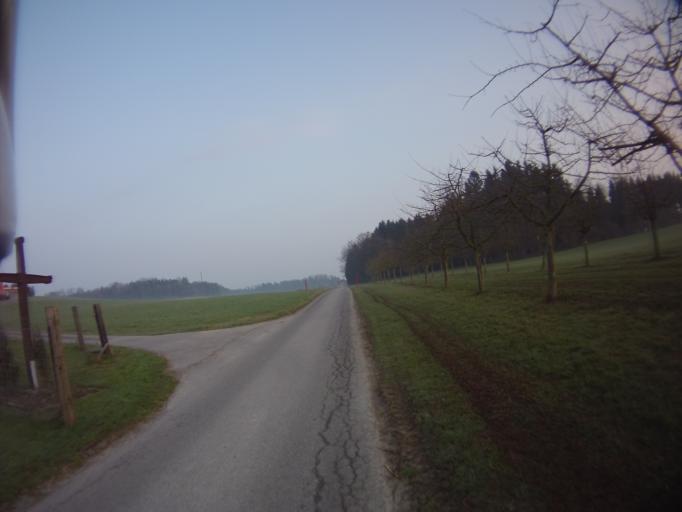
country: CH
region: Zug
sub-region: Zug
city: Cham
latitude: 47.1997
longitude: 8.4488
